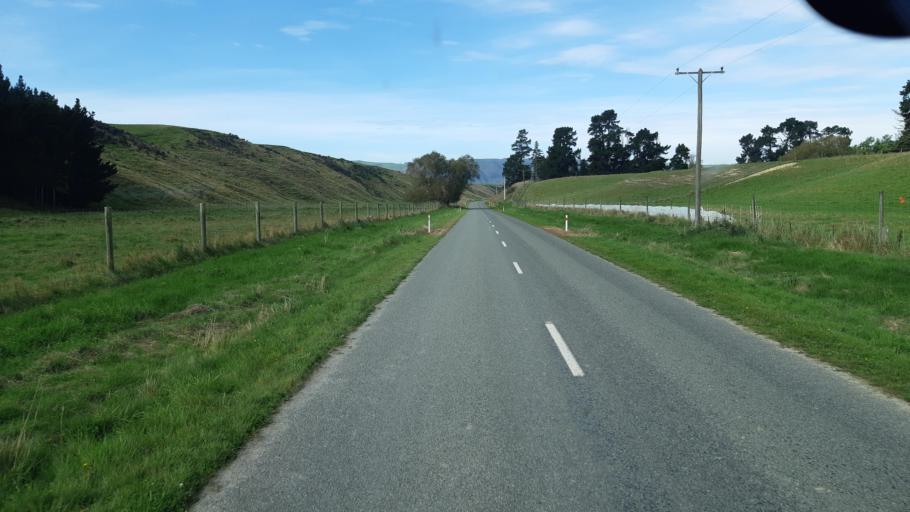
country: NZ
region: Canterbury
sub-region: Timaru District
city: Pleasant Point
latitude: -44.2121
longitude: 170.8138
